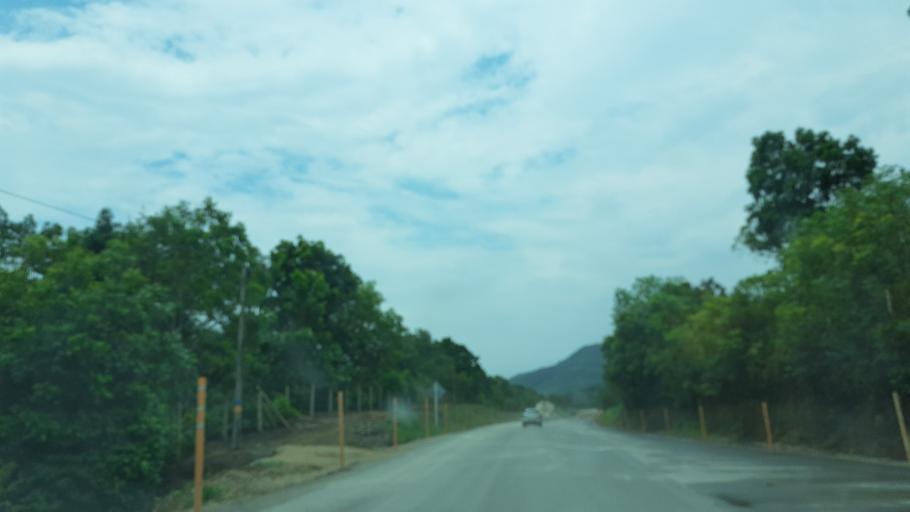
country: CO
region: Casanare
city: Sabanalarga
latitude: 4.7712
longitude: -73.0041
